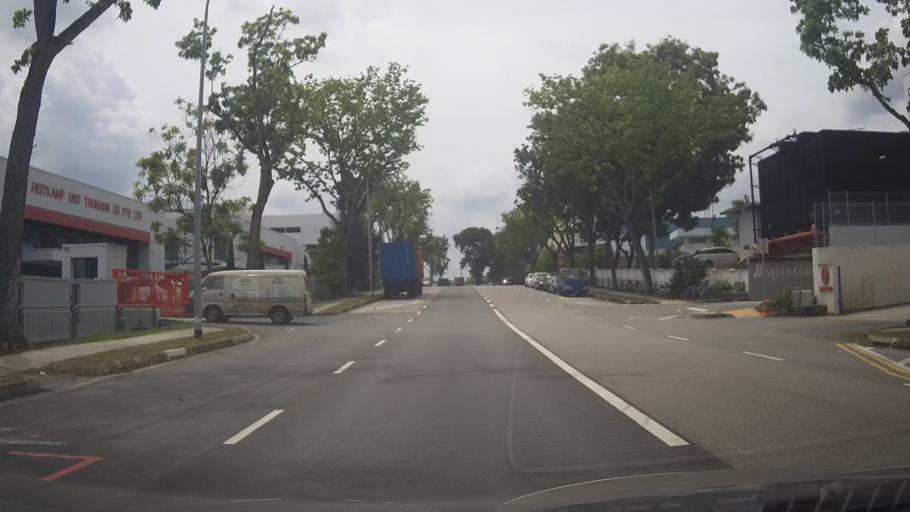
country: MY
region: Johor
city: Johor Bahru
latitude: 1.4561
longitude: 103.8033
